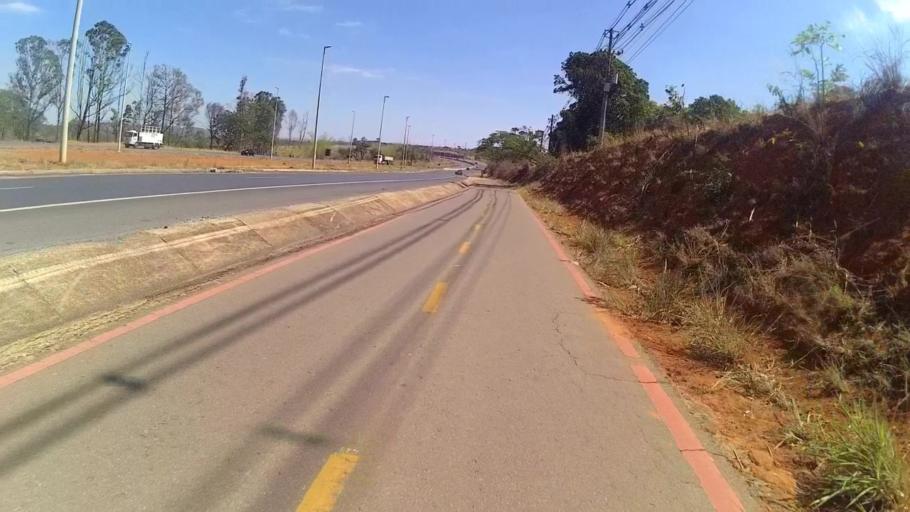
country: BR
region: Federal District
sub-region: Brasilia
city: Brasilia
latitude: -15.6565
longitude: -47.8458
